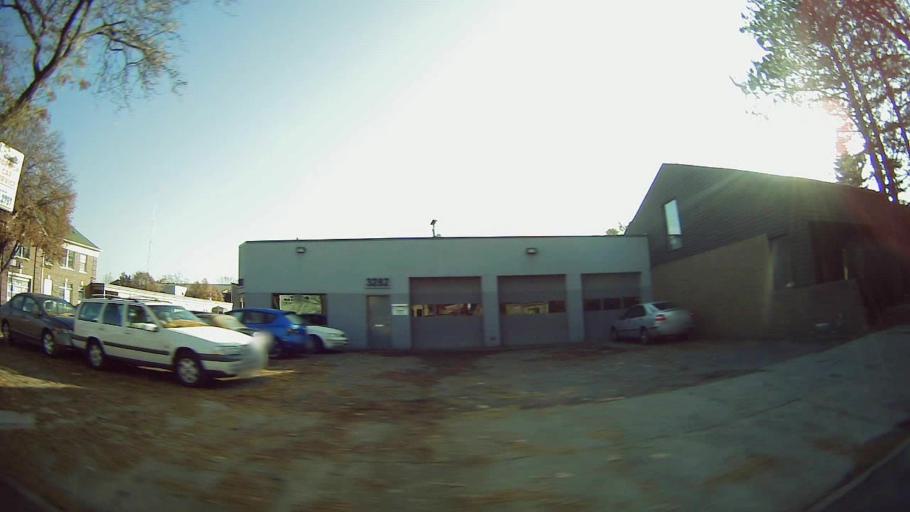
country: US
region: Michigan
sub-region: Oakland County
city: Berkley
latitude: 42.5022
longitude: -83.1838
